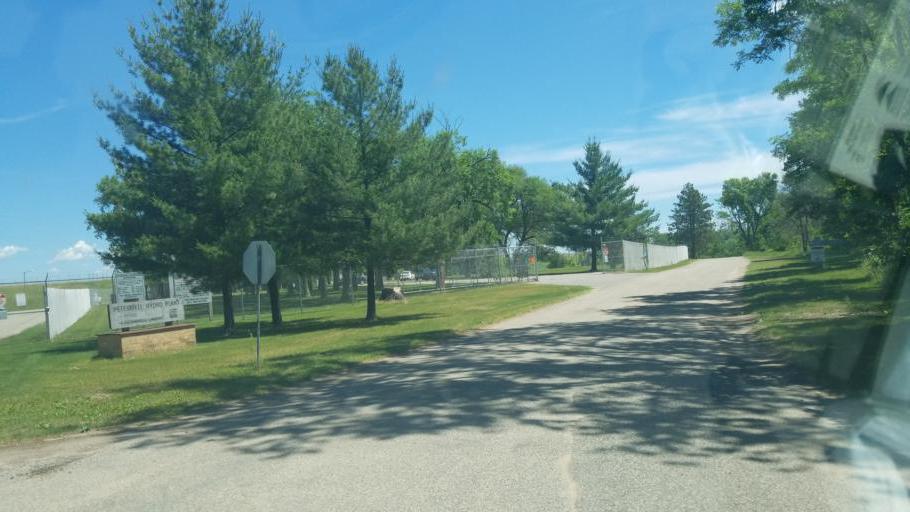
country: US
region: Wisconsin
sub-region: Adams County
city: Friendship
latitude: 44.0559
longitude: -90.0246
